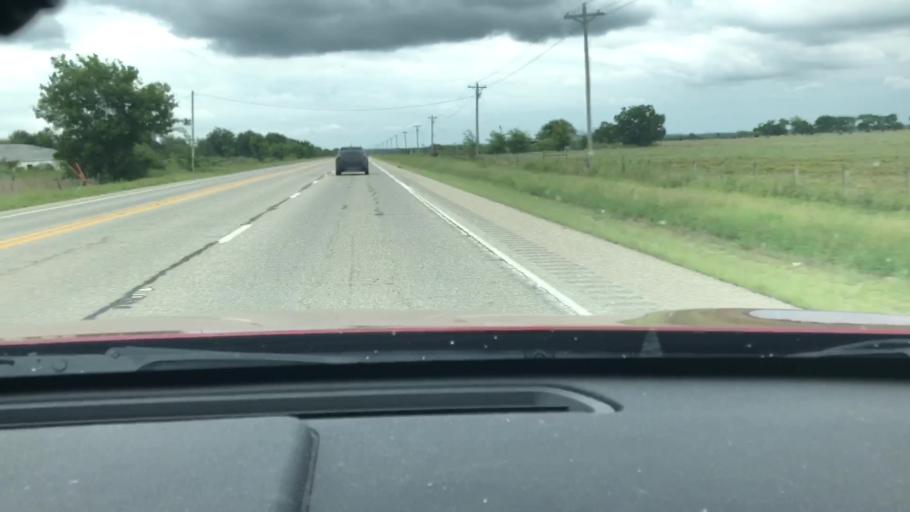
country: US
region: Arkansas
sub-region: Lafayette County
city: Lewisville
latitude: 33.4125
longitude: -93.7931
